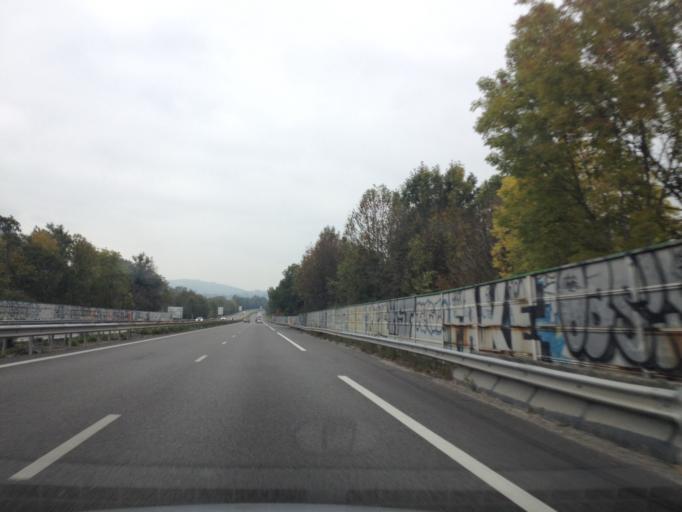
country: FR
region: Rhone-Alpes
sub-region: Departement de la Savoie
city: Gresy-sur-Aix
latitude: 45.7248
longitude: 5.9241
